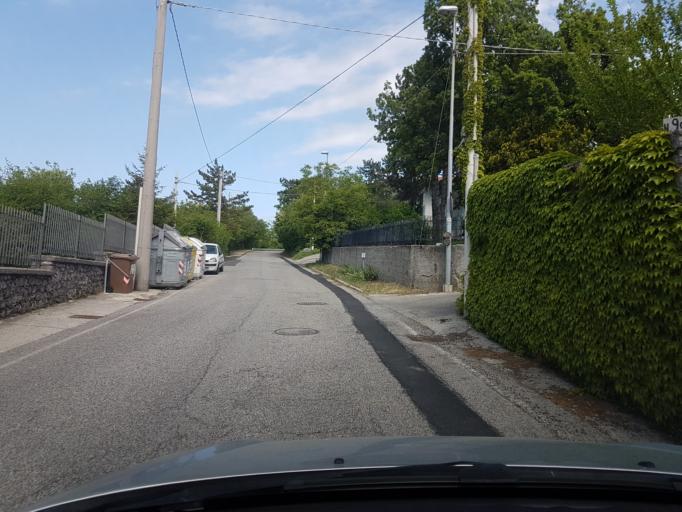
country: IT
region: Friuli Venezia Giulia
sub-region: Provincia di Trieste
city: Sistiana-Visogliano
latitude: 45.7793
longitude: 13.6482
